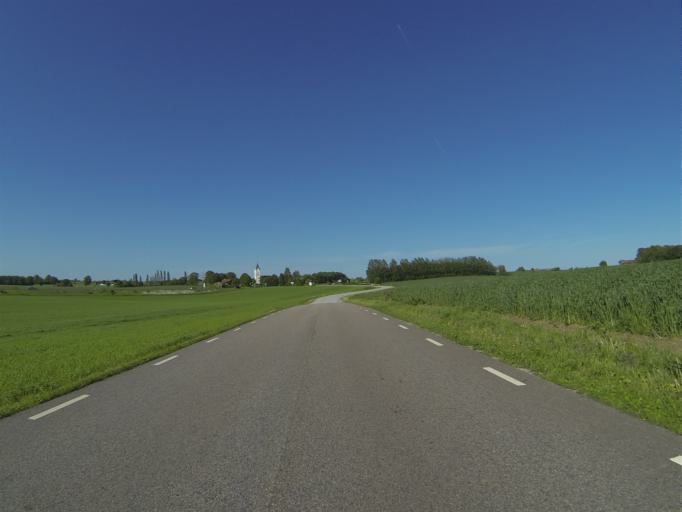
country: SE
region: Skane
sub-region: Staffanstorps Kommun
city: Hjaerup
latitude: 55.6172
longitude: 13.1559
